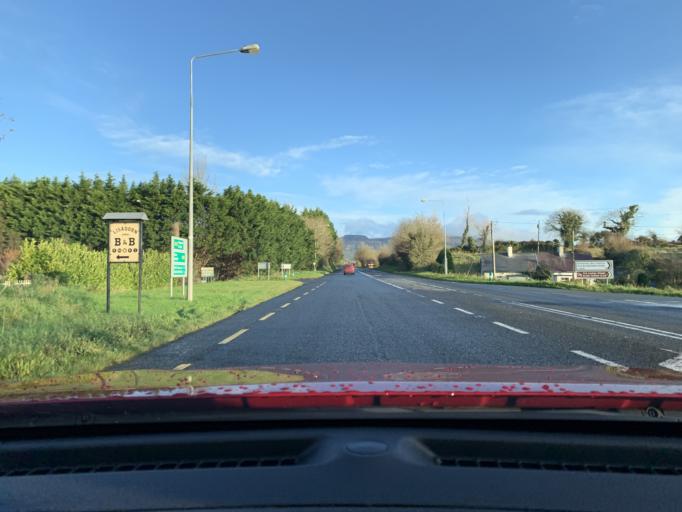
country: IE
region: Connaught
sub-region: Sligo
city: Sligo
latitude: 54.2943
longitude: -8.4733
